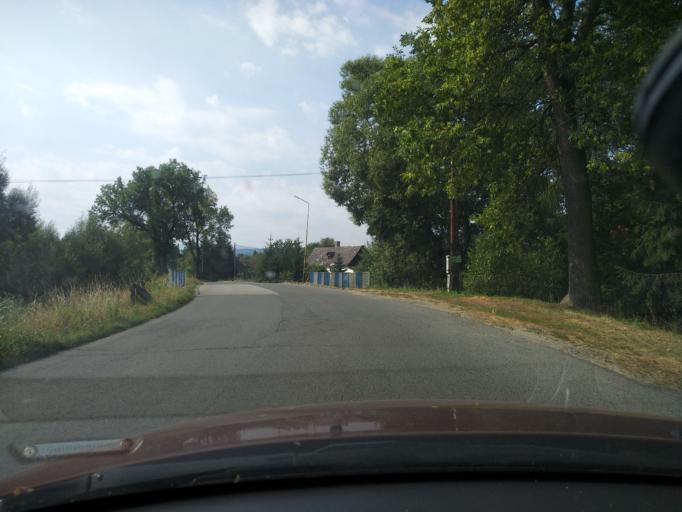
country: PL
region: Lower Silesian Voivodeship
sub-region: Powiat jeleniogorski
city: Stara Kamienica
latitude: 50.9269
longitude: 15.5736
